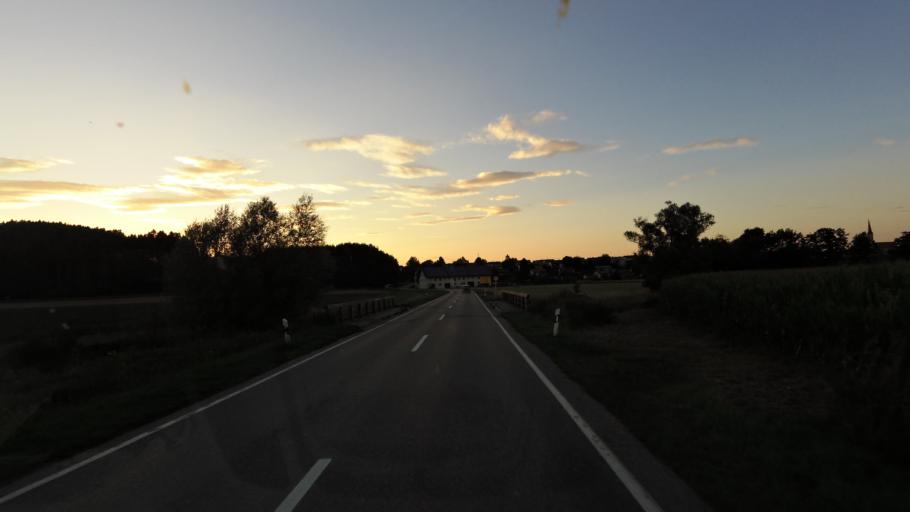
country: DE
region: Bavaria
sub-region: Upper Bavaria
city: Taufkirchen
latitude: 48.1417
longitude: 12.4528
